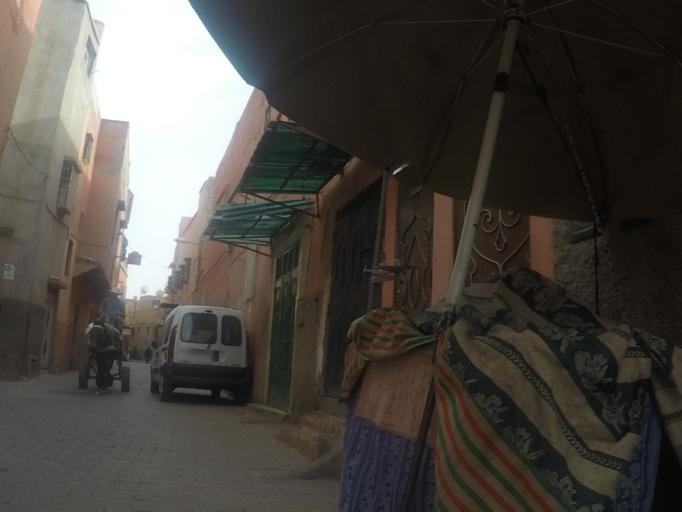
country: MA
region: Marrakech-Tensift-Al Haouz
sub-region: Marrakech
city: Marrakesh
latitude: 31.6270
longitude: -7.9812
